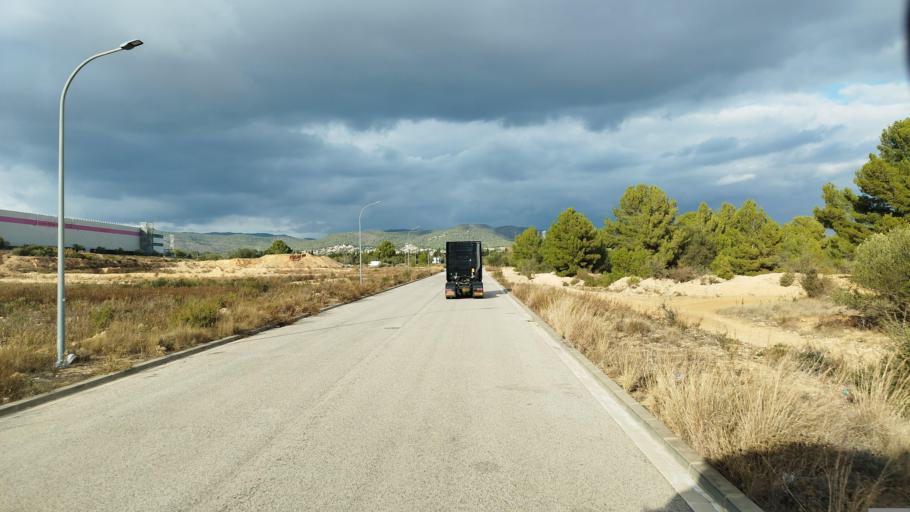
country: ES
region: Catalonia
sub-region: Provincia de Tarragona
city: Santa Oliva
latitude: 41.2706
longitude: 1.5236
